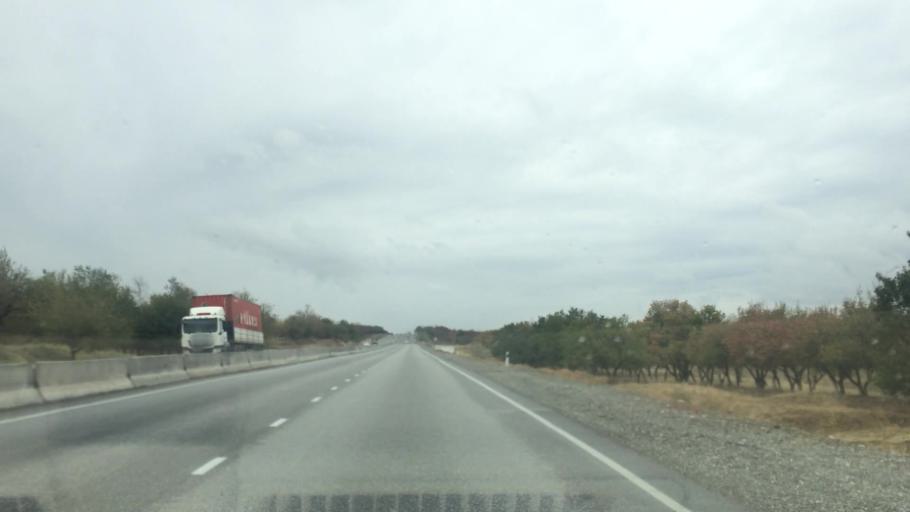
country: UZ
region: Samarqand
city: Bulung'ur
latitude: 39.8652
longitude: 67.4737
